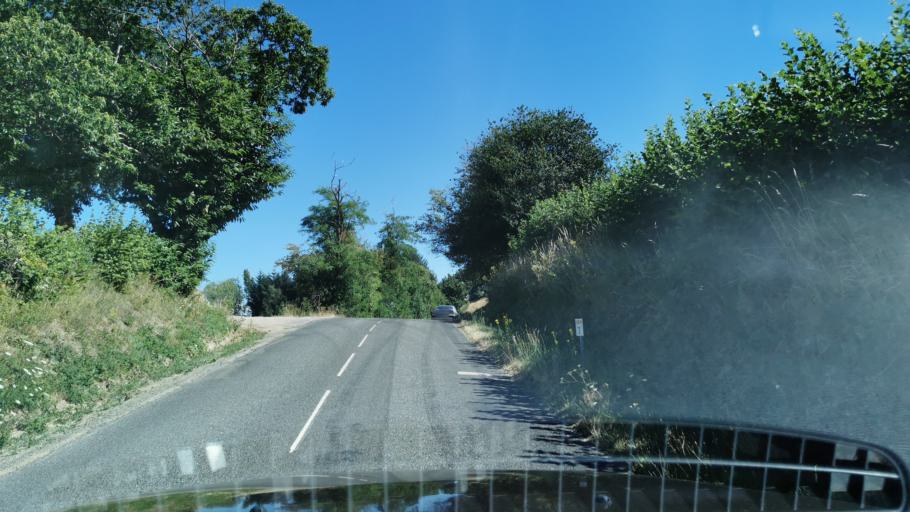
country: FR
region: Bourgogne
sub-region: Departement de Saone-et-Loire
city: Montcenis
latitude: 46.8022
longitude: 4.3585
